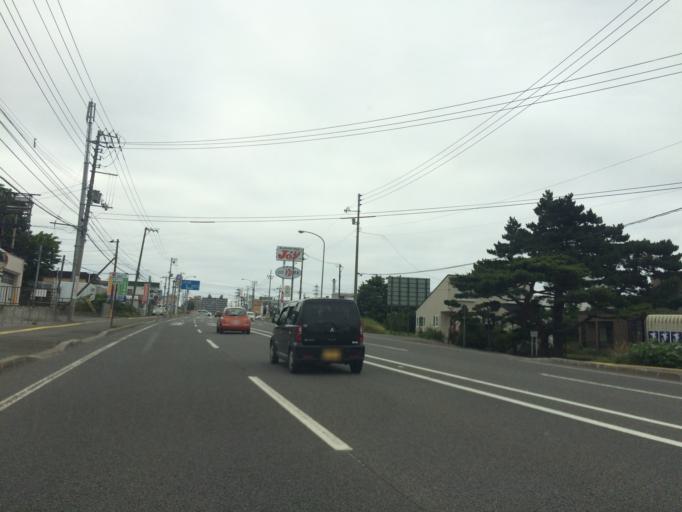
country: JP
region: Hokkaido
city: Sapporo
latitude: 43.1269
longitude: 141.2165
